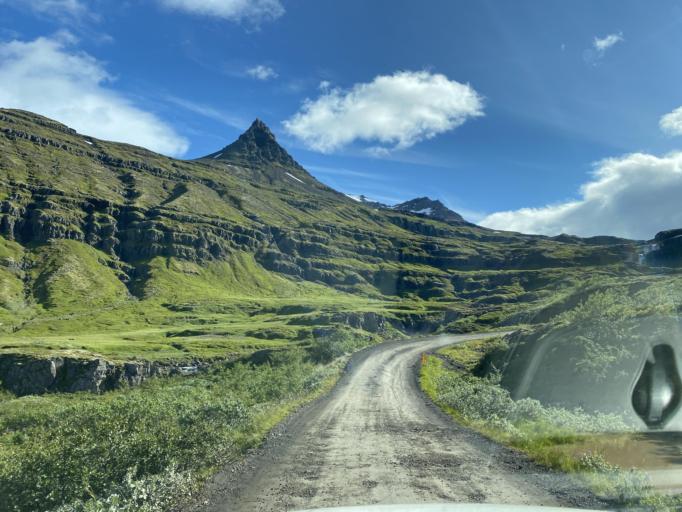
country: IS
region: East
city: Eskifjoerdur
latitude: 65.1826
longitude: -14.0726
